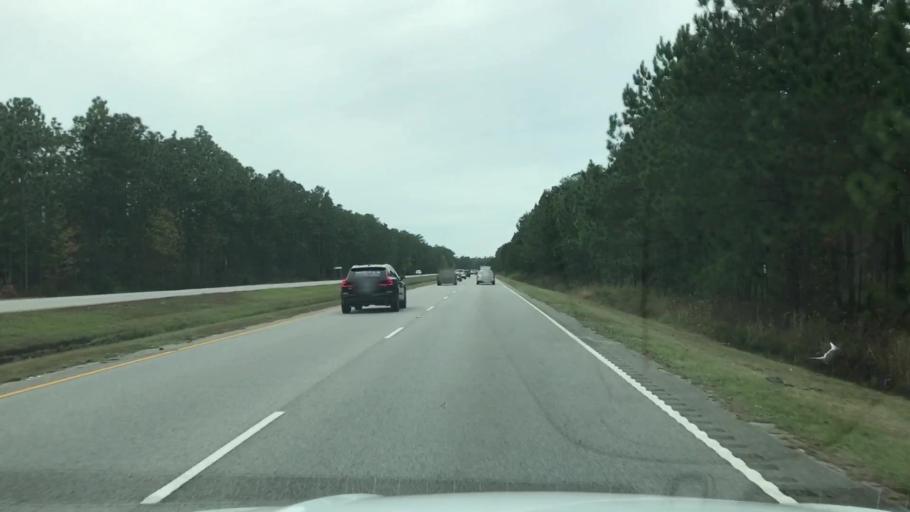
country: US
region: South Carolina
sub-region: Georgetown County
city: Georgetown
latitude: 33.4109
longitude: -79.1907
